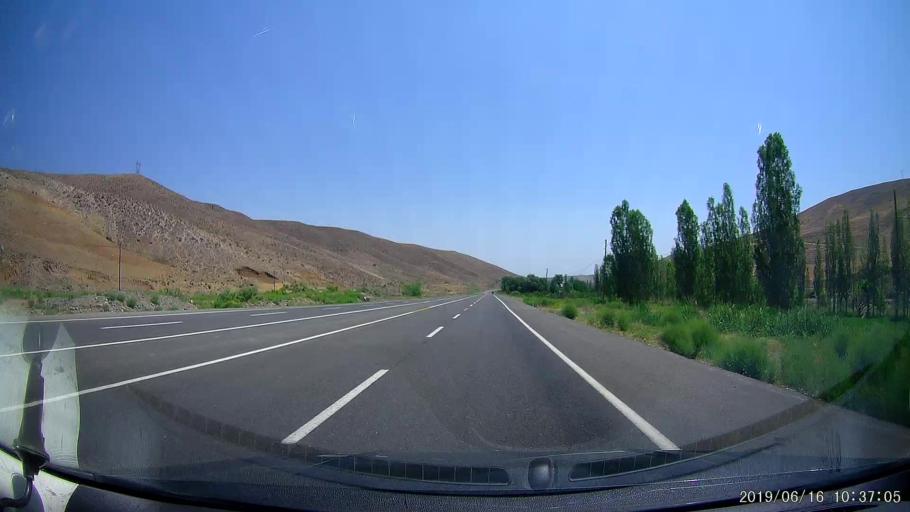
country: TR
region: Igdir
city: Tuzluca
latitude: 40.0441
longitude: 43.6922
